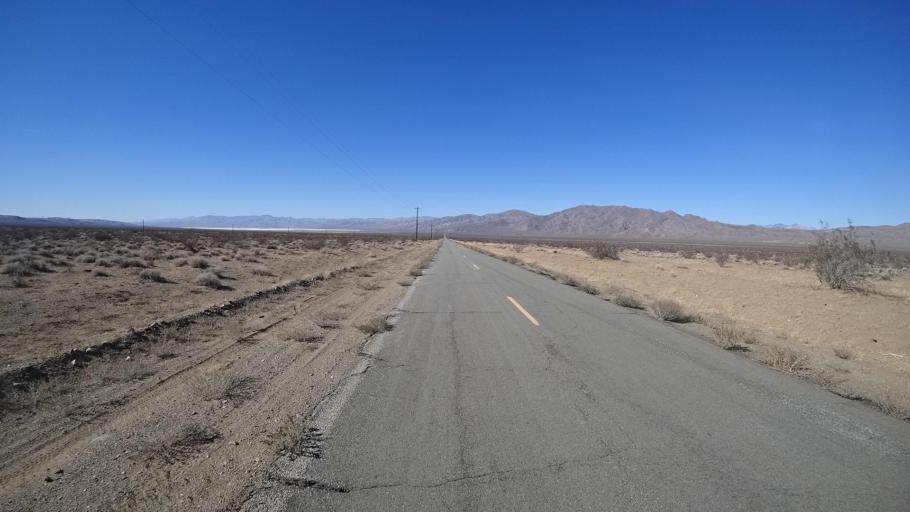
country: US
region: California
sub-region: Kern County
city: Ridgecrest
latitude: 35.3843
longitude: -117.7164
